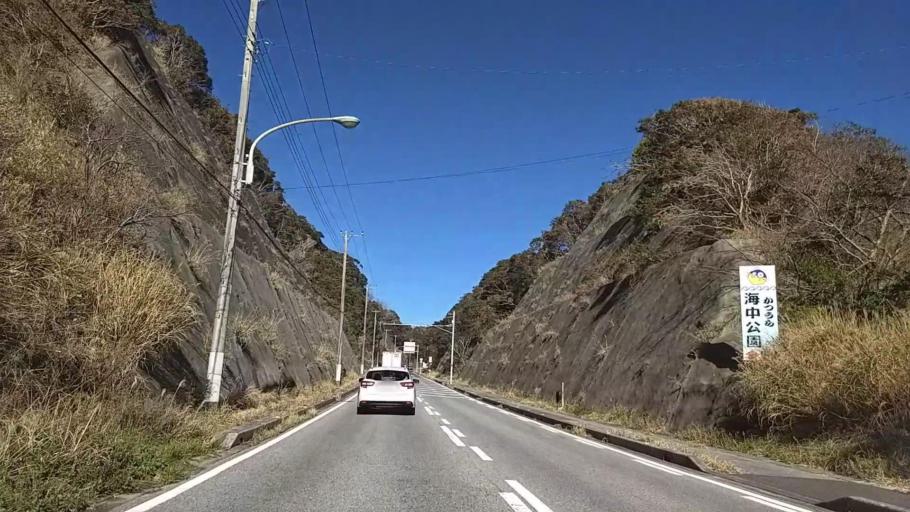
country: JP
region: Chiba
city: Katsuura
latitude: 35.1198
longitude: 140.2285
